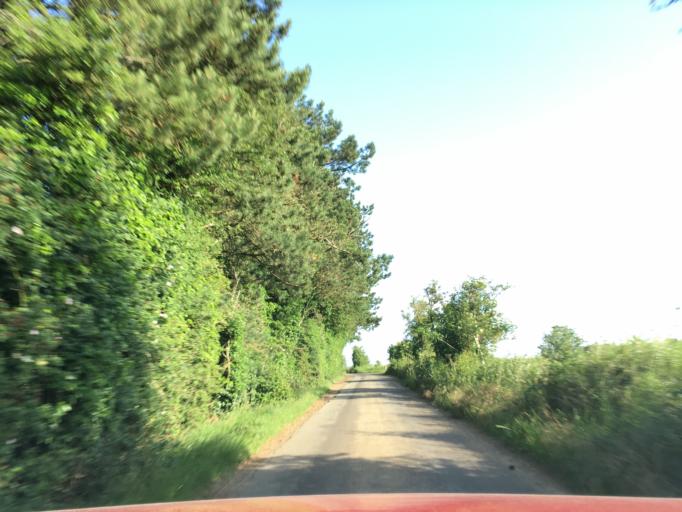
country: GB
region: England
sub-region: Oxfordshire
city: Burford
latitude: 51.7786
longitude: -1.7039
